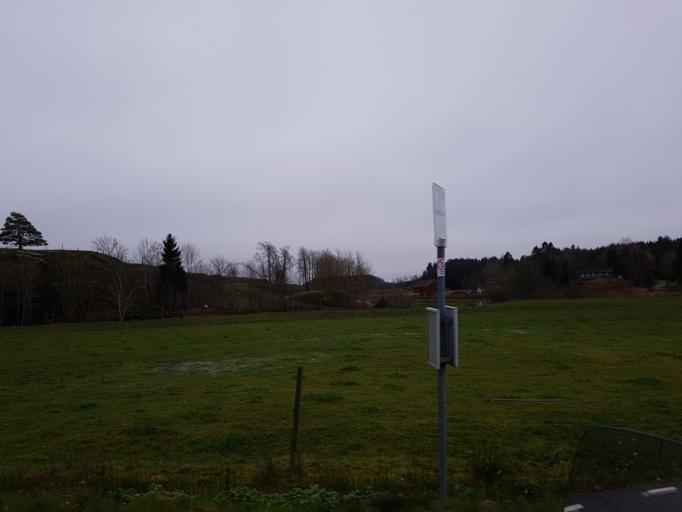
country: SE
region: Vaestra Goetaland
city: Svanesund
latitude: 58.2077
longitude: 11.7706
